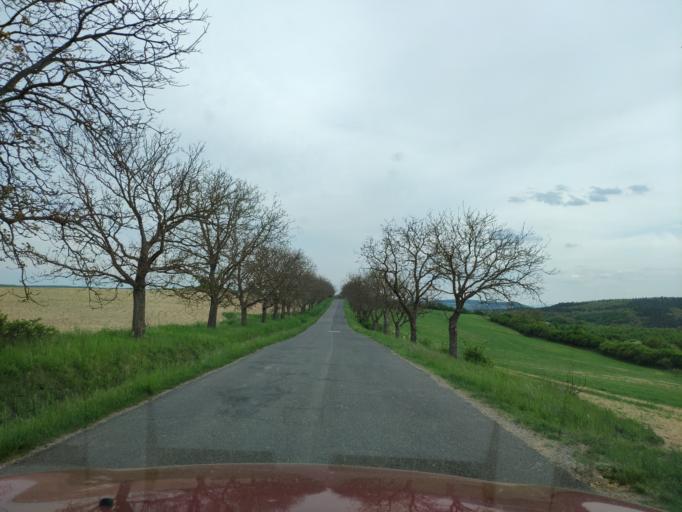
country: SK
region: Banskobystricky
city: Revuca
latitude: 48.4951
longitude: 20.2452
